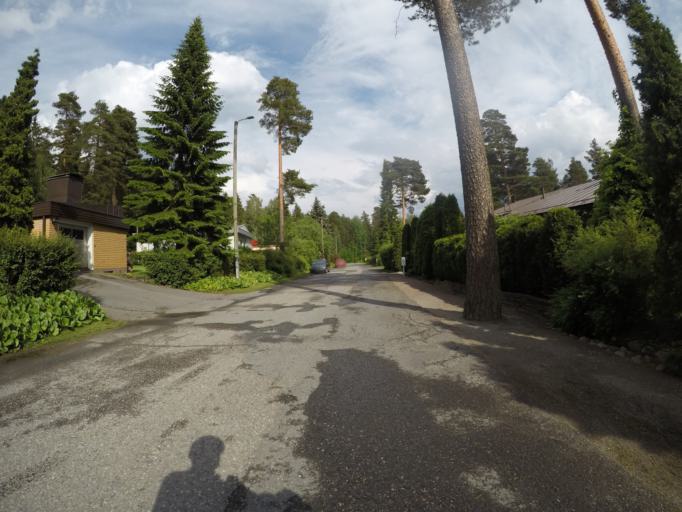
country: FI
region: Haeme
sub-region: Haemeenlinna
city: Haemeenlinna
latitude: 61.0150
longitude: 24.4726
